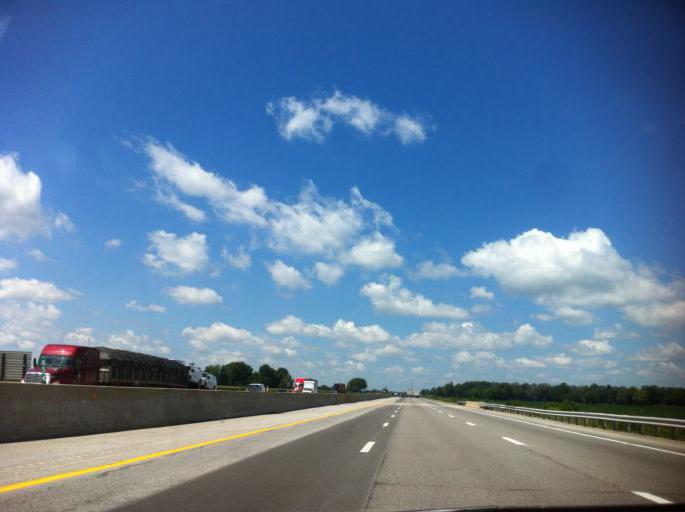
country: US
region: Ohio
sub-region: Ottawa County
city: Elmore
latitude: 41.4364
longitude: -83.2230
